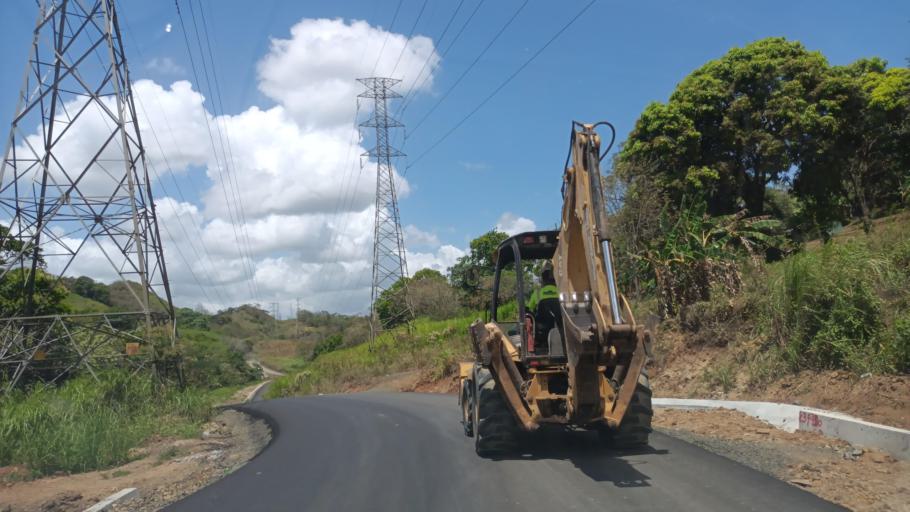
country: PA
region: Panama
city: Alcalde Diaz
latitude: 9.0821
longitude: -79.5763
